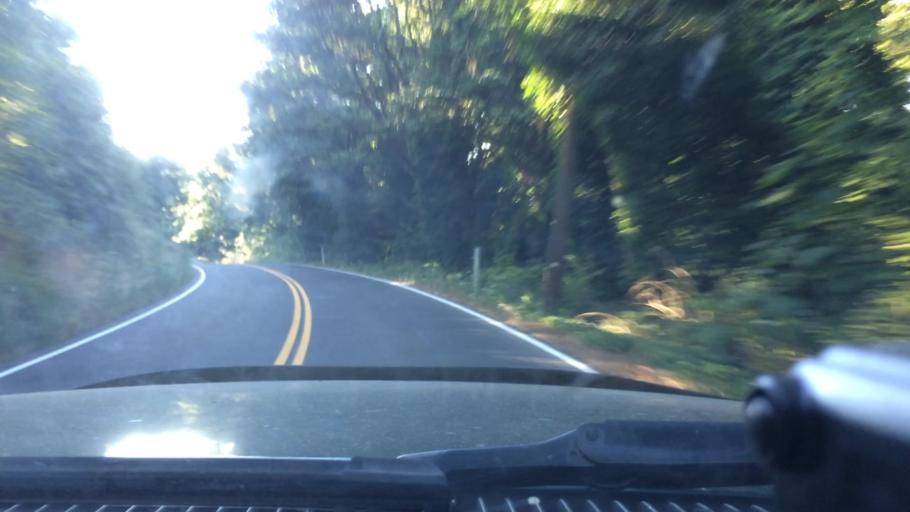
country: US
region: Oregon
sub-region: Yamhill County
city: Newberg
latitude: 45.3331
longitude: -122.9329
